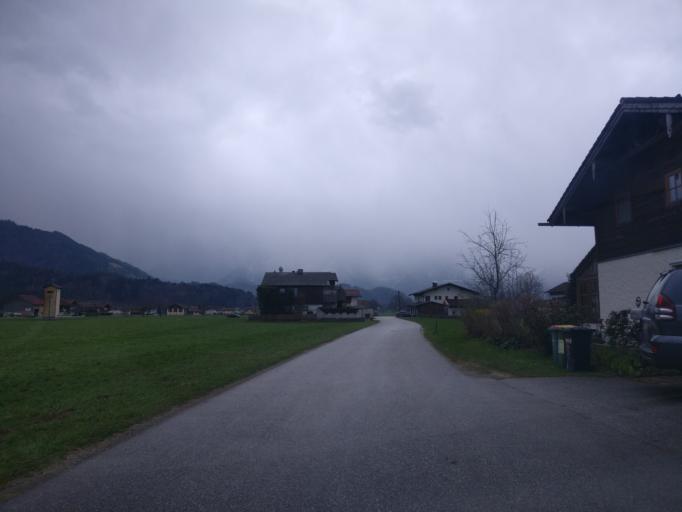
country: AT
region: Salzburg
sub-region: Politischer Bezirk Hallein
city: Kuchl
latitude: 47.6298
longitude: 13.1586
